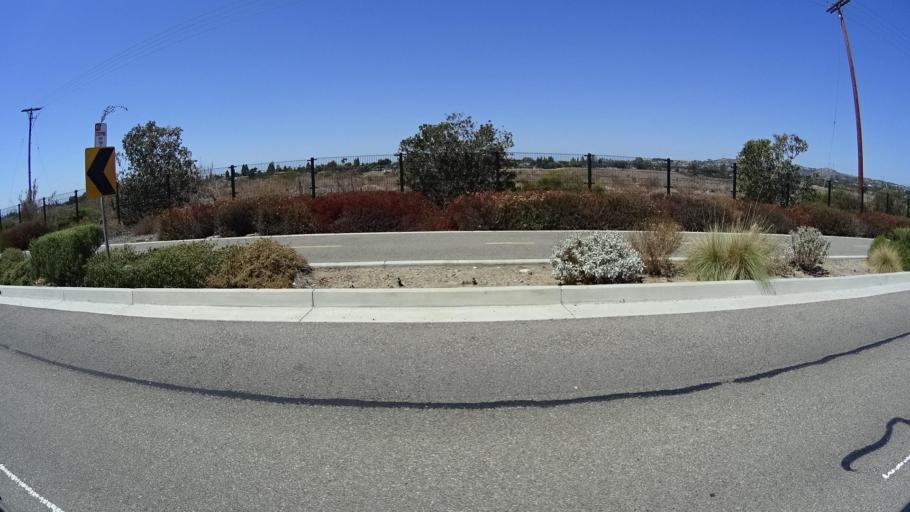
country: US
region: California
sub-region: Orange County
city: Villa Park
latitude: 33.8044
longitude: -117.8048
